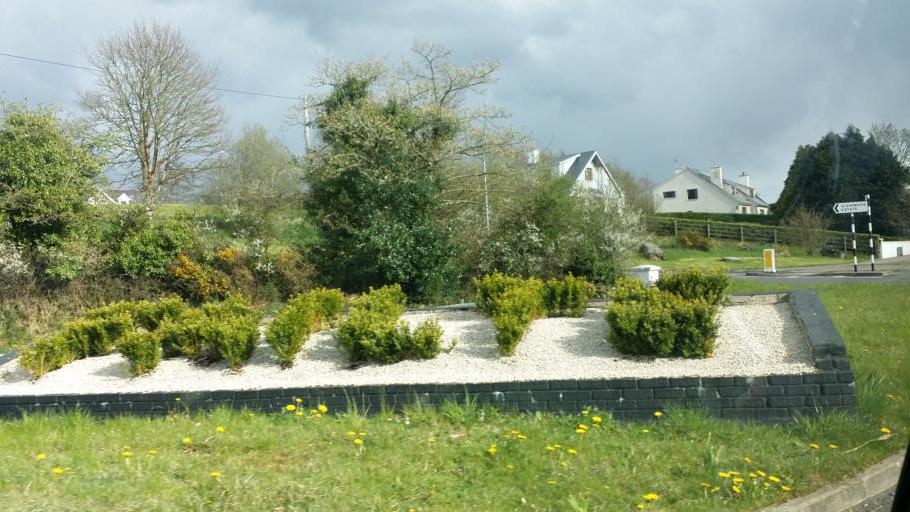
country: IE
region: Connaught
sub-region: County Leitrim
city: Manorhamilton
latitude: 54.3089
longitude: -8.1843
